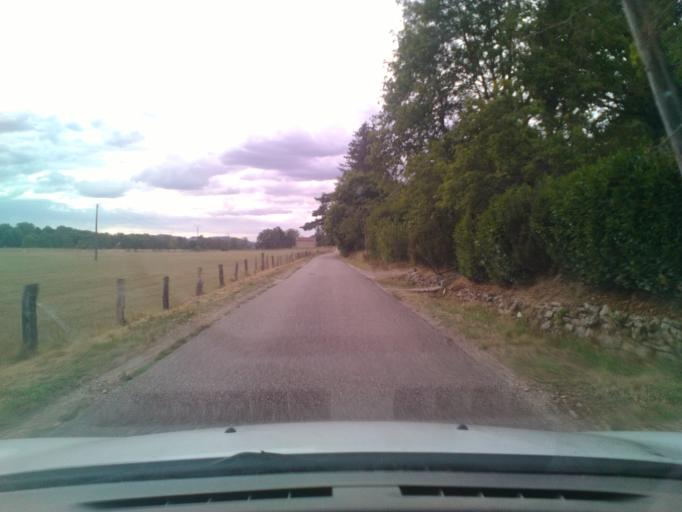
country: FR
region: Lorraine
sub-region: Departement des Vosges
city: Portieux
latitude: 48.3294
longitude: 6.3649
